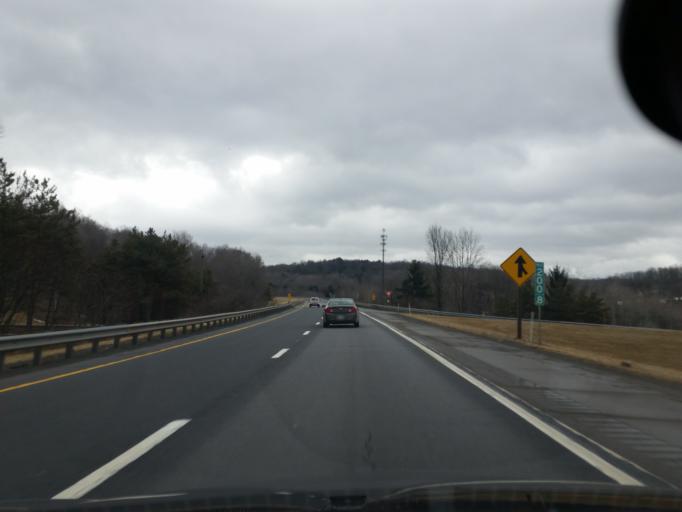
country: US
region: Pennsylvania
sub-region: Lackawanna County
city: Dalton
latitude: 41.5781
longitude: -75.6548
